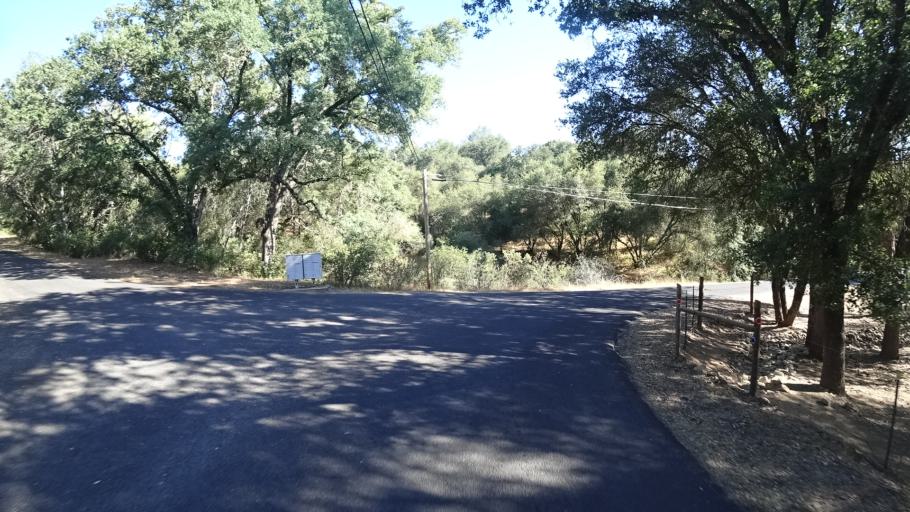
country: US
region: California
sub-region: Calaveras County
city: San Andreas
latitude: 38.2355
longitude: -120.7120
